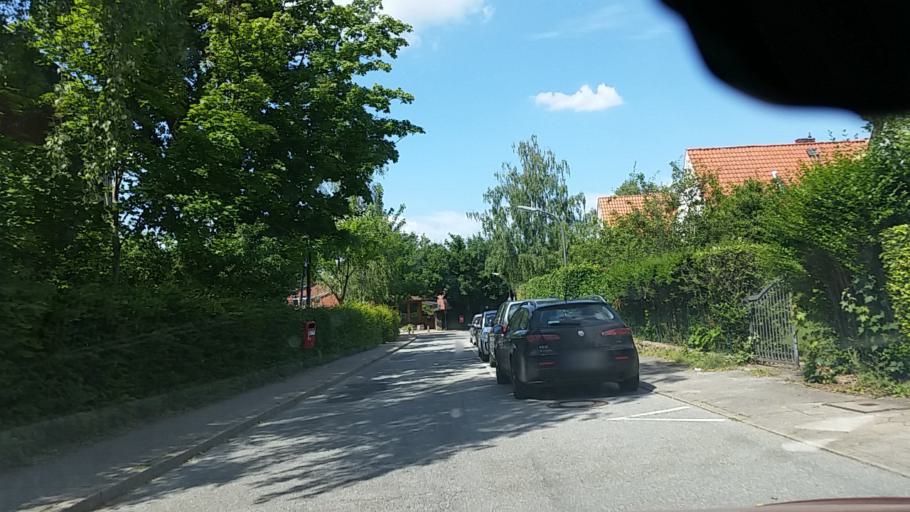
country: DE
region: Schleswig-Holstein
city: Halstenbek
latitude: 53.5707
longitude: 9.8068
